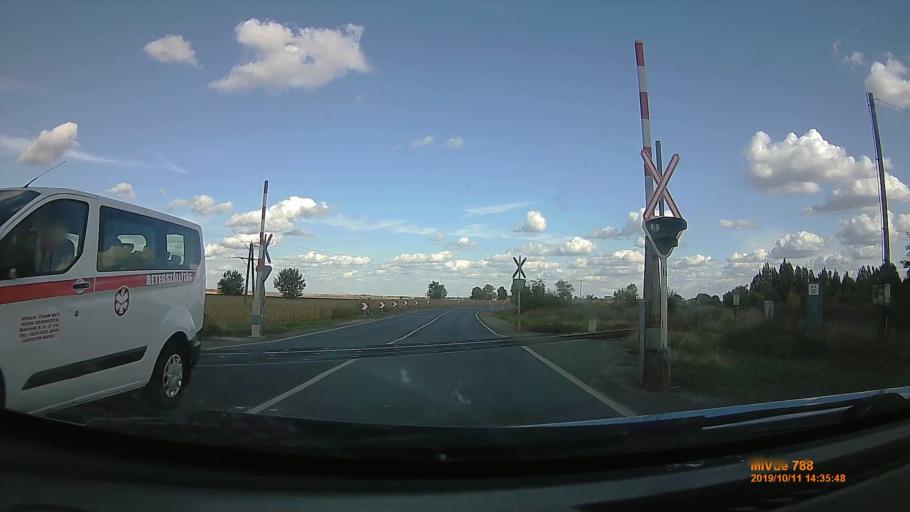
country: HU
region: Hajdu-Bihar
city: Ebes
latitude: 47.5589
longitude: 21.4987
